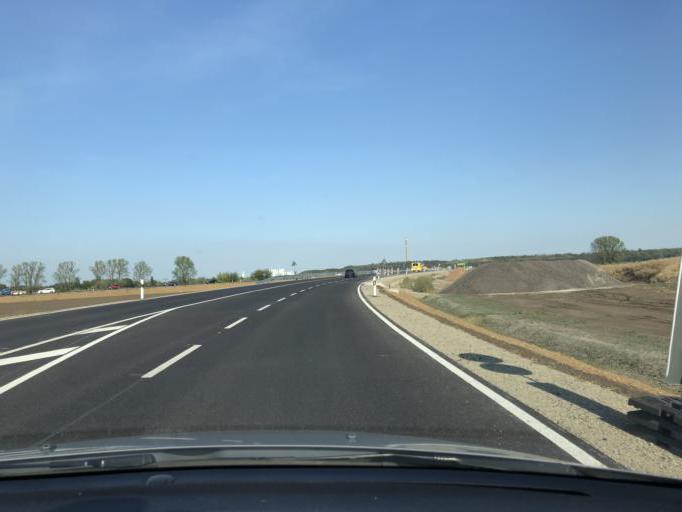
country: DE
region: Saxony-Anhalt
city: Beuna
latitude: 51.3183
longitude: 11.9603
